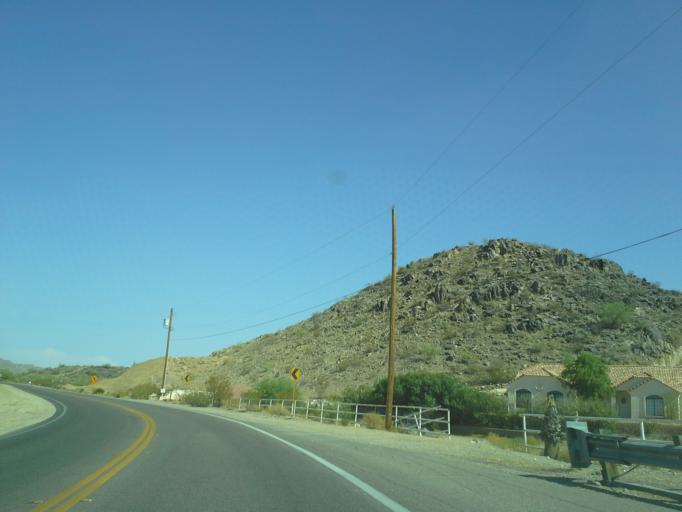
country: US
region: Arizona
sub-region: Maricopa County
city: Queen Creek
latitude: 33.2060
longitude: -111.7201
